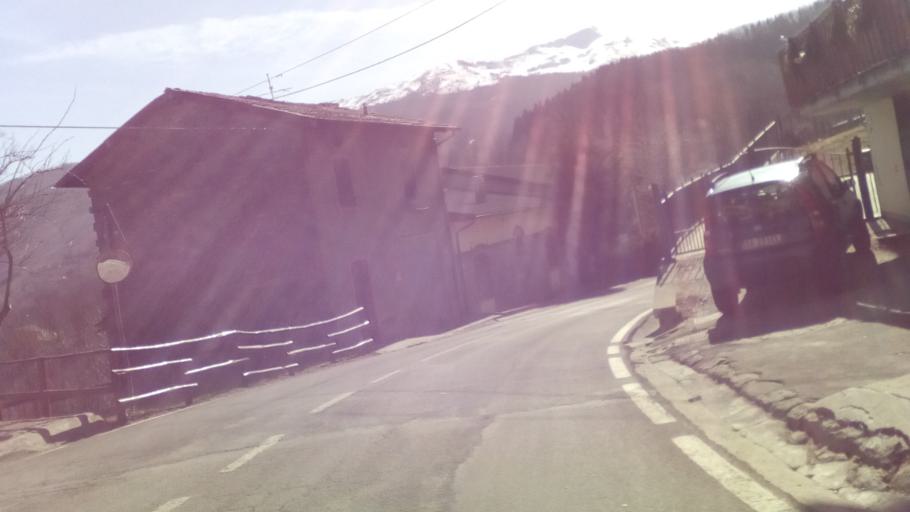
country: IT
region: Emilia-Romagna
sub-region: Provincia di Modena
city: Pievepelago
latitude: 44.1920
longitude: 10.5527
